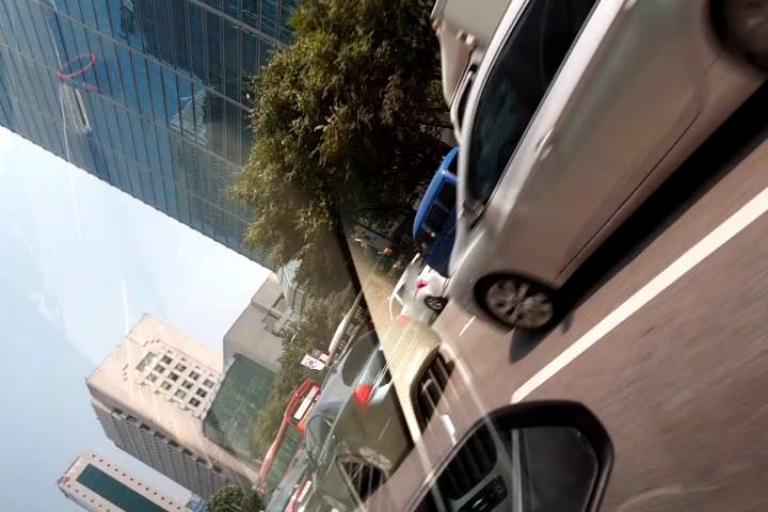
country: KR
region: Seoul
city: Seoul
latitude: 37.5004
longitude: 127.0359
